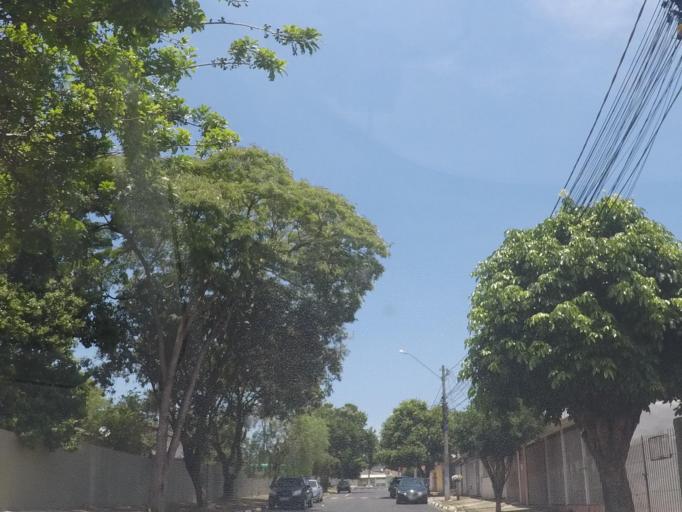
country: BR
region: Sao Paulo
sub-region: Hortolandia
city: Hortolandia
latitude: -22.8501
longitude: -47.1799
